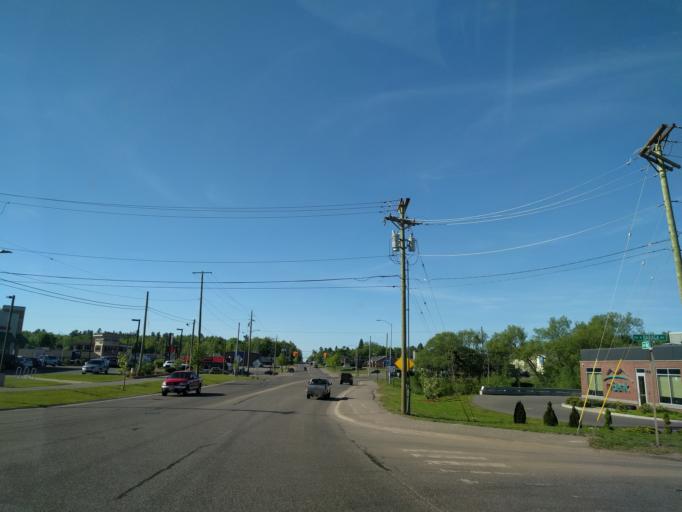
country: US
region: Michigan
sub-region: Marquette County
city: Trowbridge Park
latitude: 46.5447
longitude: -87.4199
